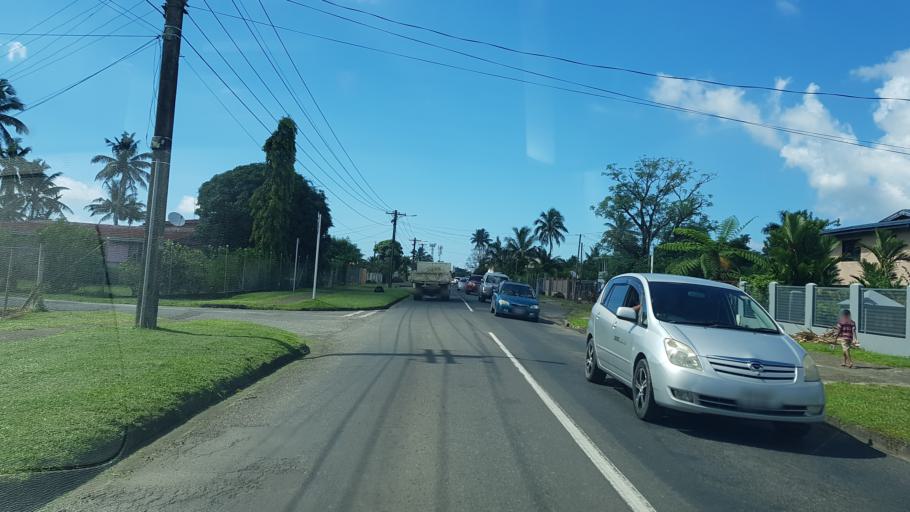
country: FJ
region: Central
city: Suva
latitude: -18.1331
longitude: 178.4591
